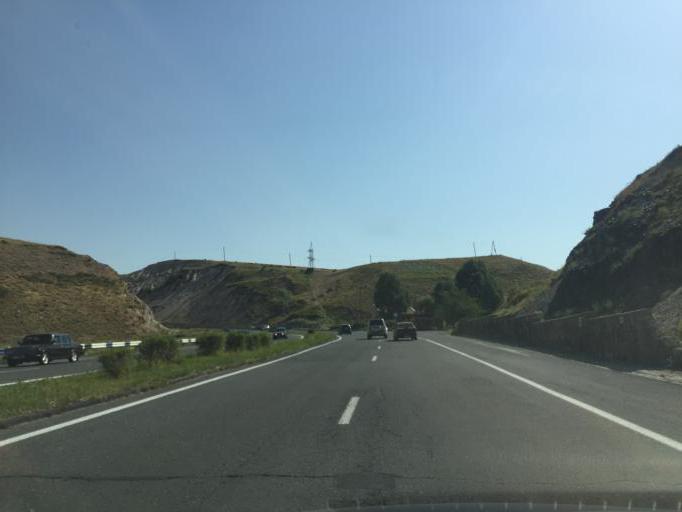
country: AM
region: Kotayk'i Marz
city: Fantan
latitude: 40.3693
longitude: 44.6483
